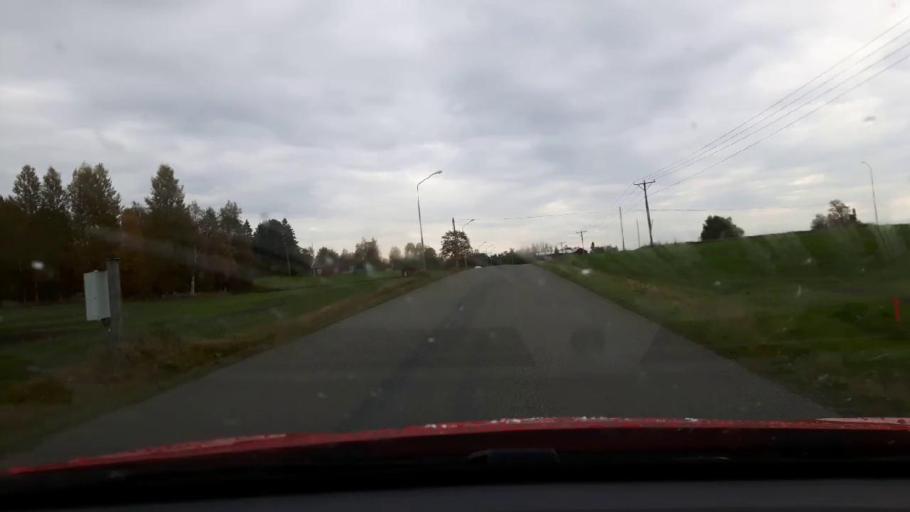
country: SE
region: Jaemtland
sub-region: Bergs Kommun
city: Hoverberg
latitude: 62.9444
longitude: 14.4955
